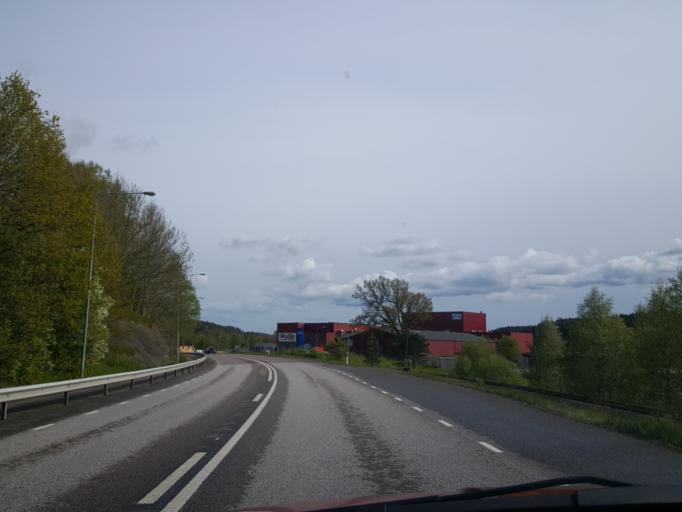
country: SE
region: Vaestra Goetaland
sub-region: Lilla Edets Kommun
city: Lilla Edet
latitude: 58.1112
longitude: 12.1433
